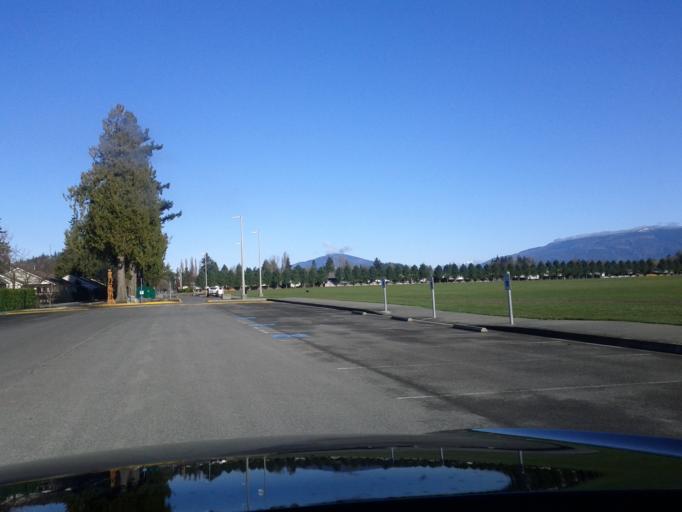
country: US
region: Washington
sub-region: Skagit County
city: Burlington
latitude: 48.4611
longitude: -122.3192
